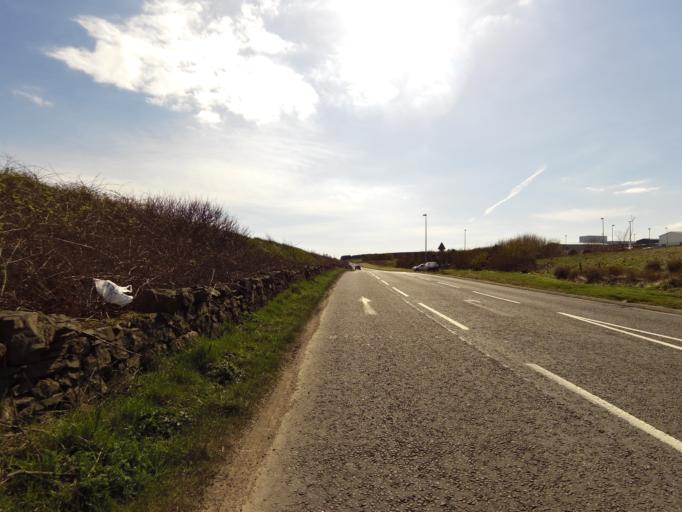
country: GB
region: Scotland
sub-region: Aberdeen City
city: Aberdeen
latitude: 57.1167
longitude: -2.0628
